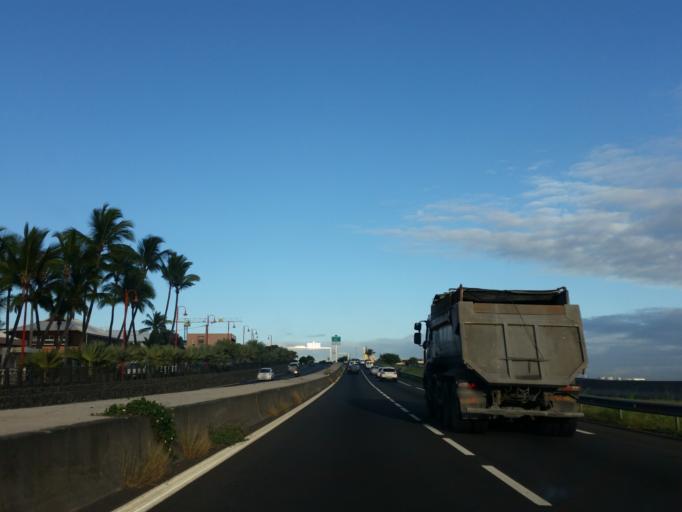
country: RE
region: Reunion
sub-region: Reunion
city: La Possession
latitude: -20.9257
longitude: 55.3366
